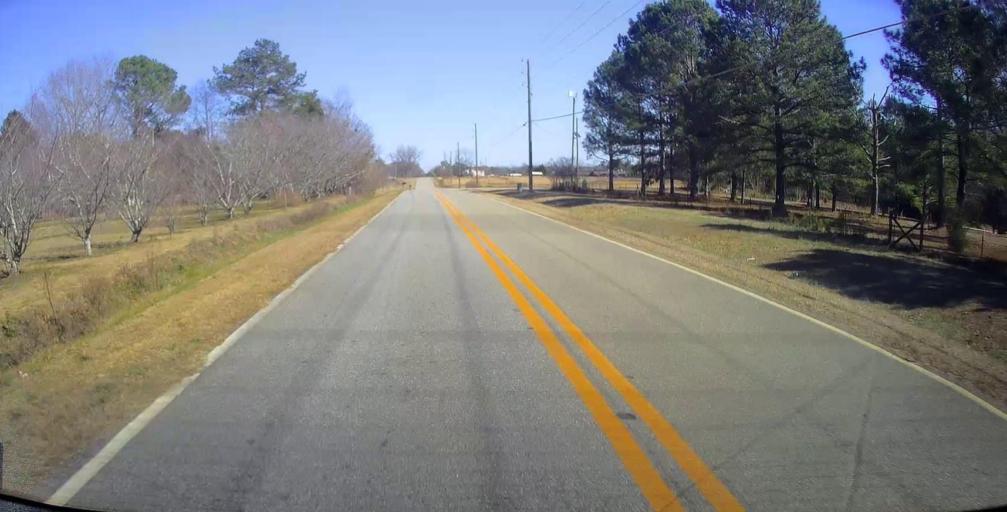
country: US
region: Georgia
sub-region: Peach County
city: Byron
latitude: 32.6191
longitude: -83.7744
